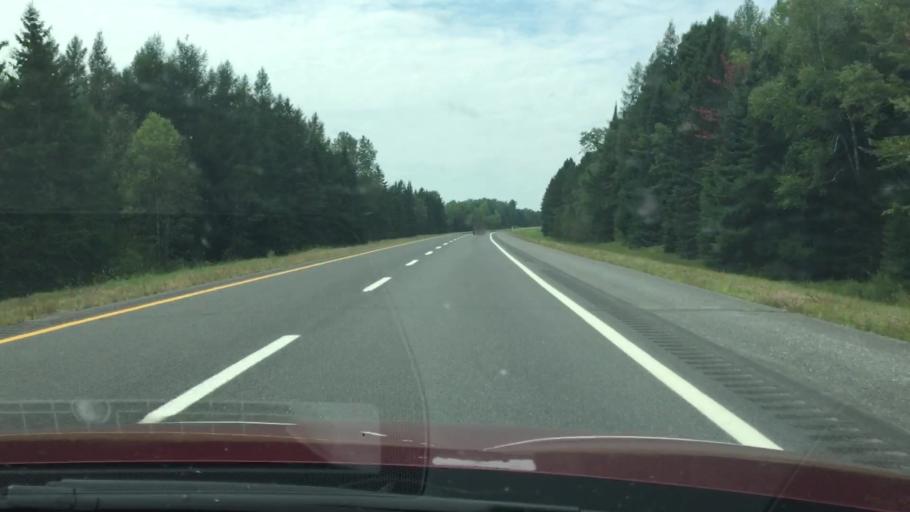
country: US
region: Maine
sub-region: Aroostook County
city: Houlton
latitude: 46.1374
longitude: -67.9060
